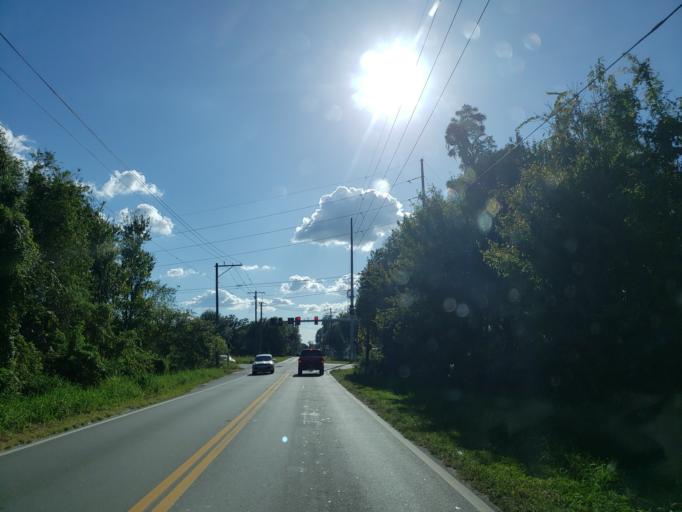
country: US
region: Florida
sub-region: Hillsborough County
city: Dover
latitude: 27.9866
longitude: -82.1698
